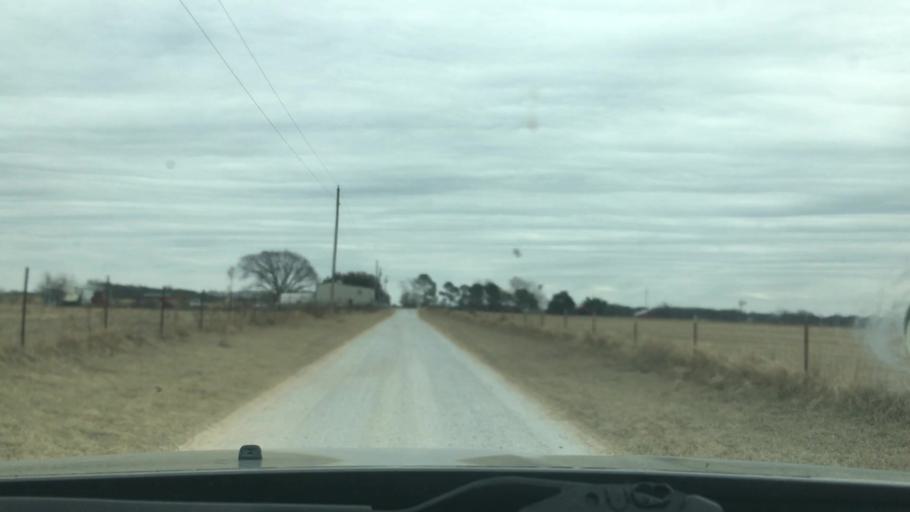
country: US
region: Texas
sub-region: Cooke County
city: Lindsay
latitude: 33.7807
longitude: -97.1636
